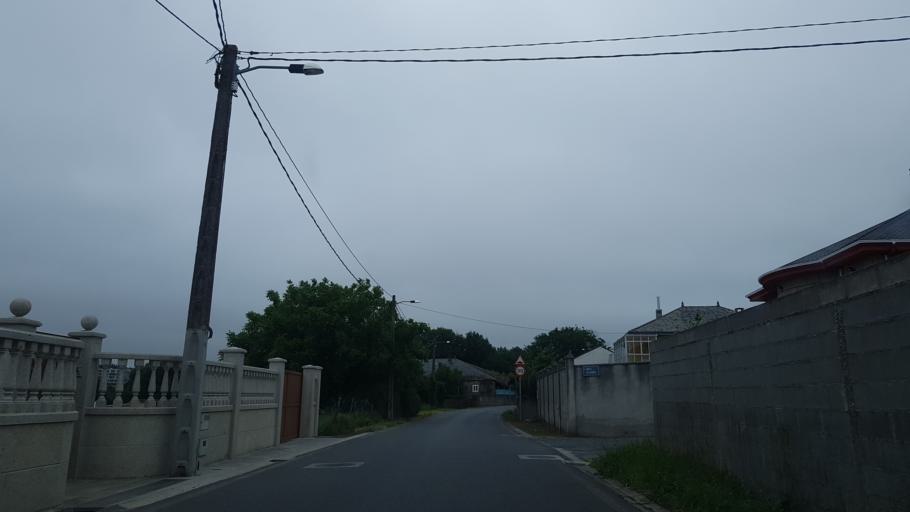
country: ES
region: Galicia
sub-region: Provincia de Lugo
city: Lugo
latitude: 43.0350
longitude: -7.5596
